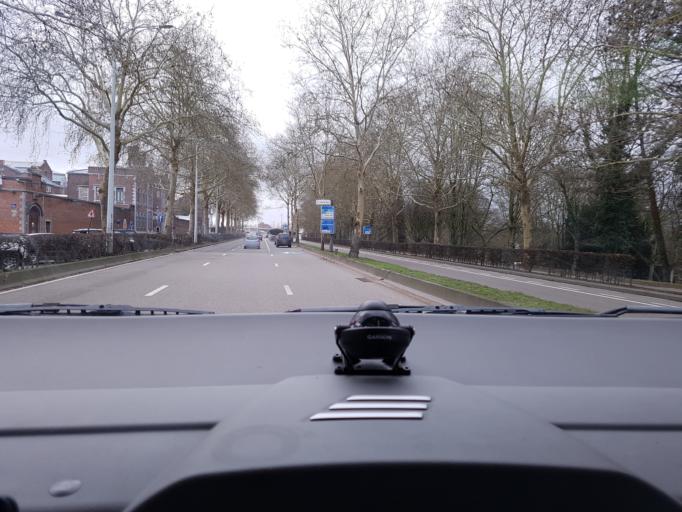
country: BE
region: Wallonia
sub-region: Province du Hainaut
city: Mons
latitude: 50.4612
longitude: 3.9528
